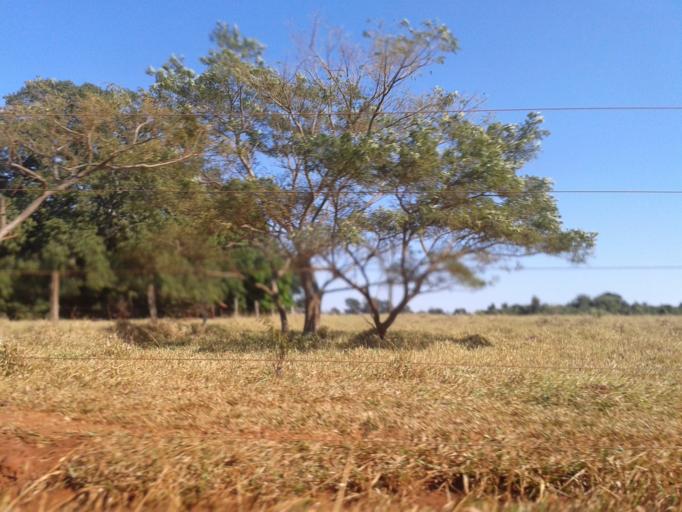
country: BR
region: Minas Gerais
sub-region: Centralina
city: Centralina
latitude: -18.7318
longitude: -49.1779
